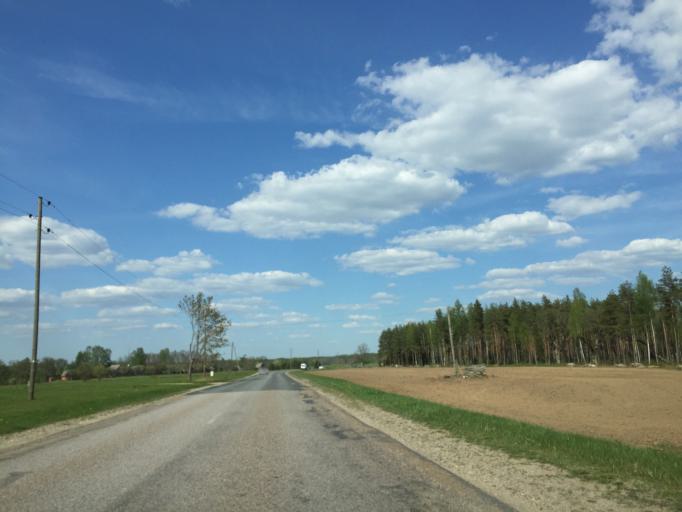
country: LV
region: Limbazu Rajons
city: Limbazi
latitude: 57.4254
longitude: 24.7078
